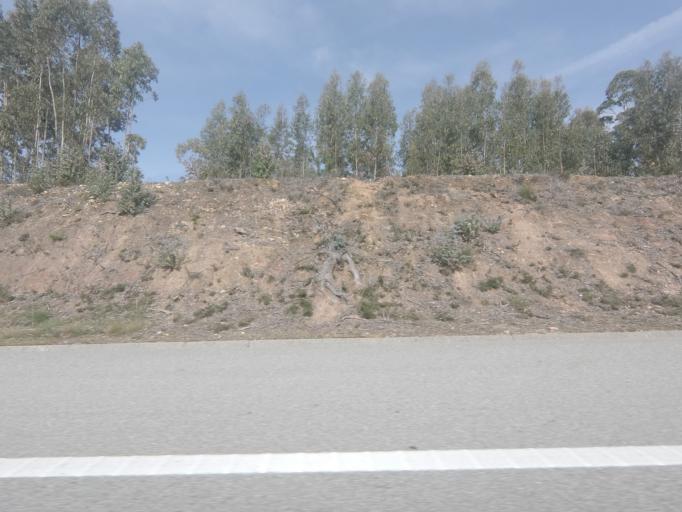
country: PT
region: Aveiro
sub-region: Agueda
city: Valongo
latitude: 40.6603
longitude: -8.3874
